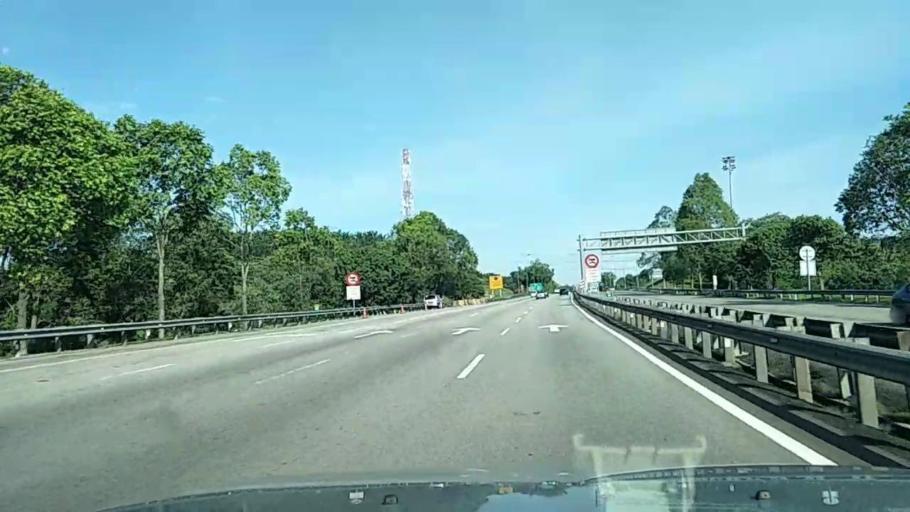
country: MY
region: Negeri Sembilan
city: Kampung Baharu Nilai
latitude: 2.8503
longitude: 101.7828
